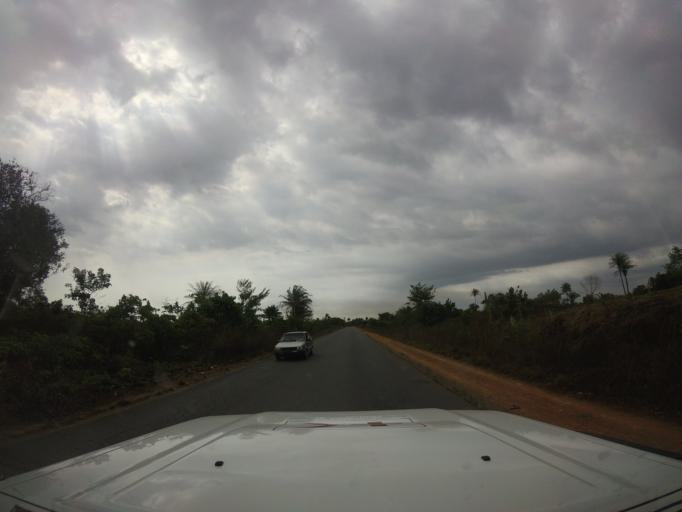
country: LR
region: Montserrado
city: Monrovia
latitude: 6.5180
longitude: -10.8272
